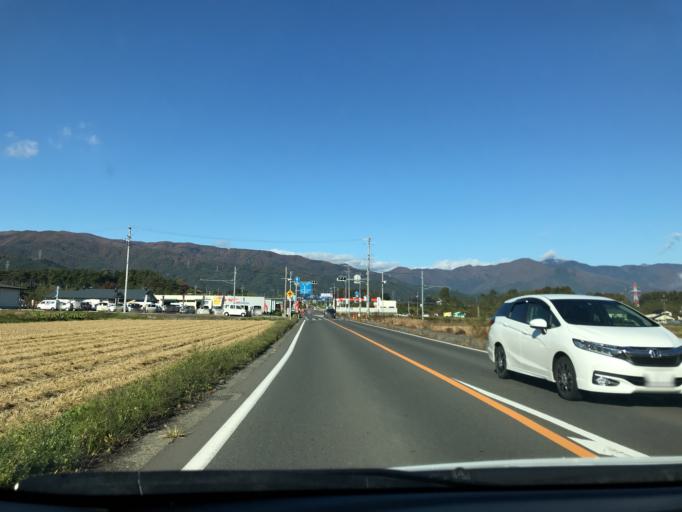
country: JP
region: Nagano
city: Shiojiri
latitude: 36.1487
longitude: 137.9048
